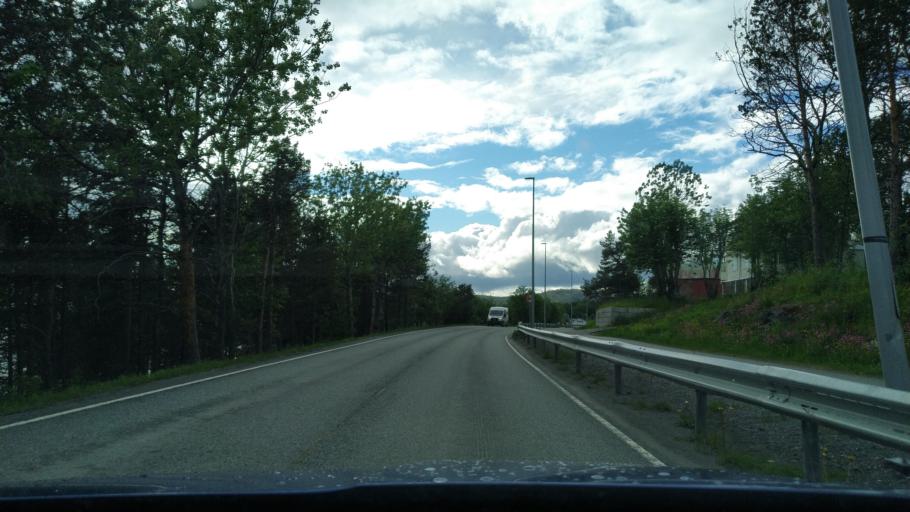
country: NO
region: Troms
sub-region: Sorreisa
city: Sorreisa
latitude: 69.1778
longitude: 18.0755
